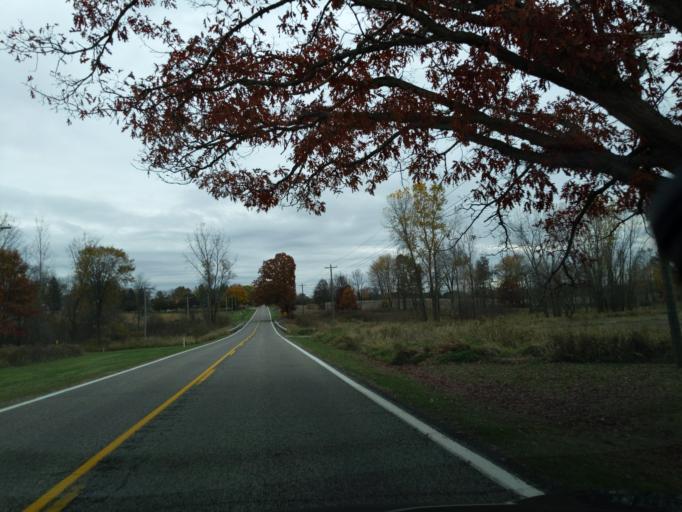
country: US
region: Michigan
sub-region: Eaton County
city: Eaton Rapids
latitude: 42.4823
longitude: -84.6010
